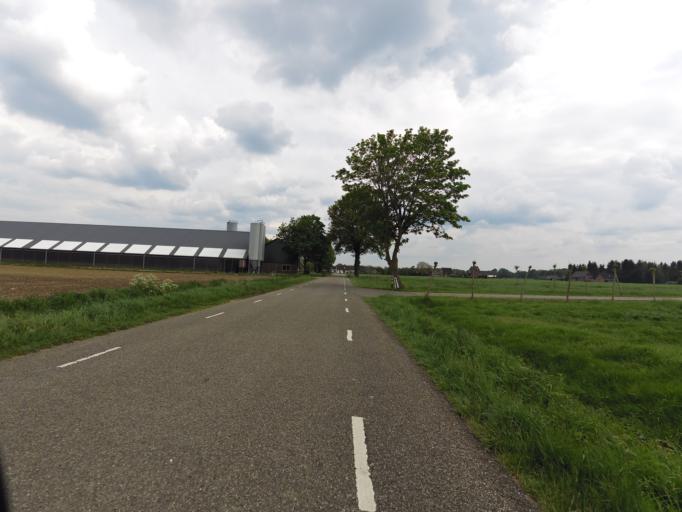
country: NL
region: Gelderland
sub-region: Gemeente Doetinchem
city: Doetinchem
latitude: 51.9393
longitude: 6.2535
